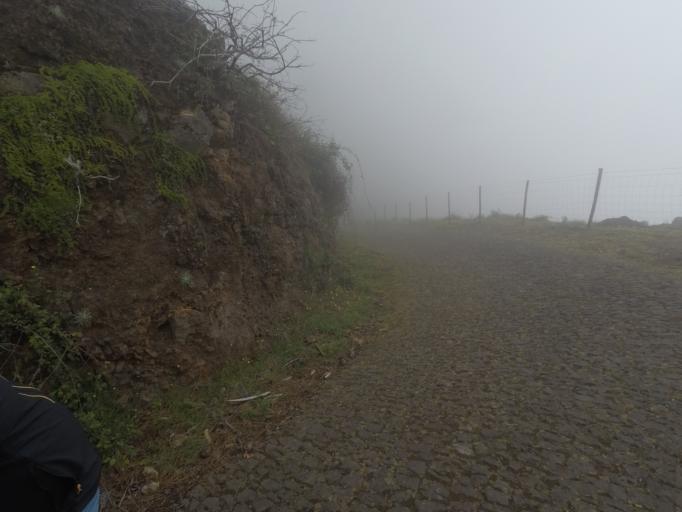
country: PT
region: Madeira
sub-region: Calheta
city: Arco da Calheta
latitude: 32.7311
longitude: -17.0973
